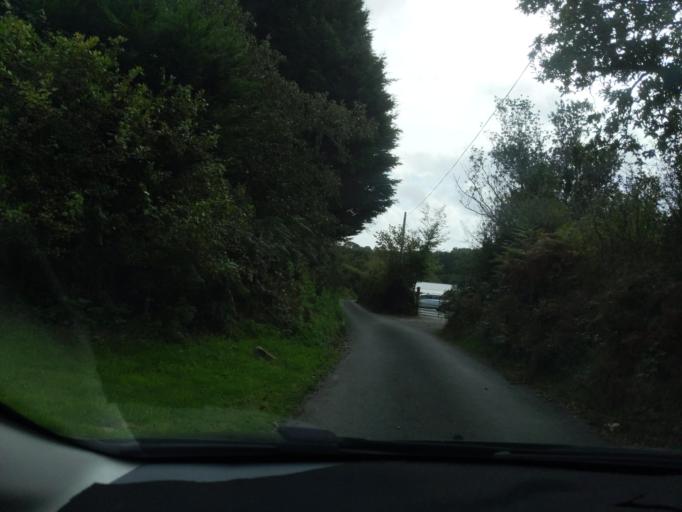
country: GB
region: England
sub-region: Cornwall
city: Lostwithiel
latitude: 50.3980
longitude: -4.7036
